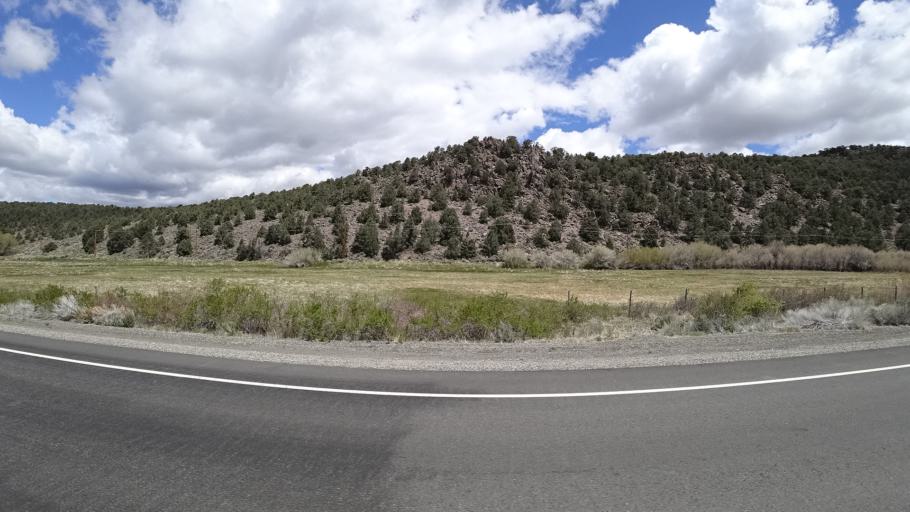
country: US
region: California
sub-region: Mono County
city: Bridgeport
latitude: 38.1941
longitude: -119.2142
